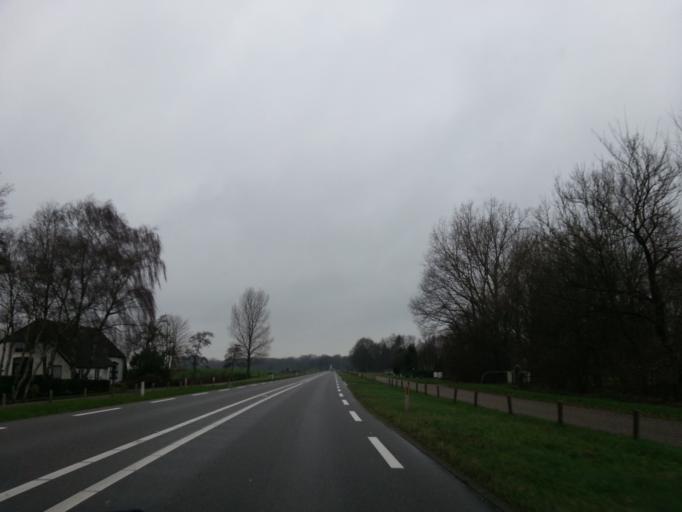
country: NL
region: Overijssel
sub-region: Gemeente Zwolle
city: Zwolle
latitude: 52.5248
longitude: 6.1674
